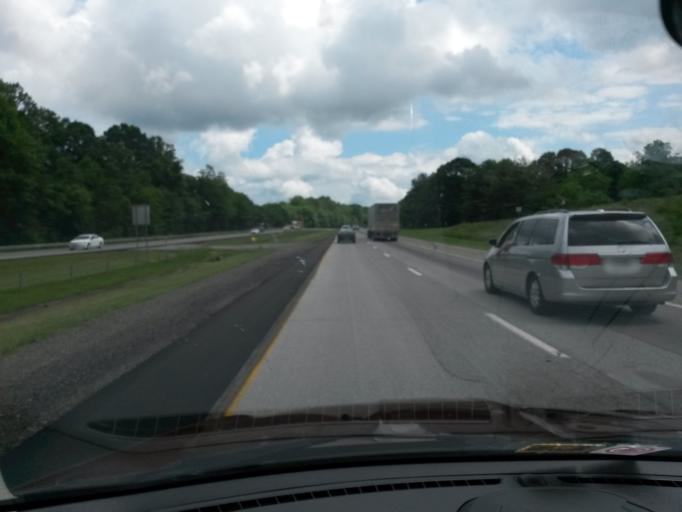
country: US
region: Virginia
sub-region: Carroll County
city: Cana
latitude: 36.5590
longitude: -80.7444
